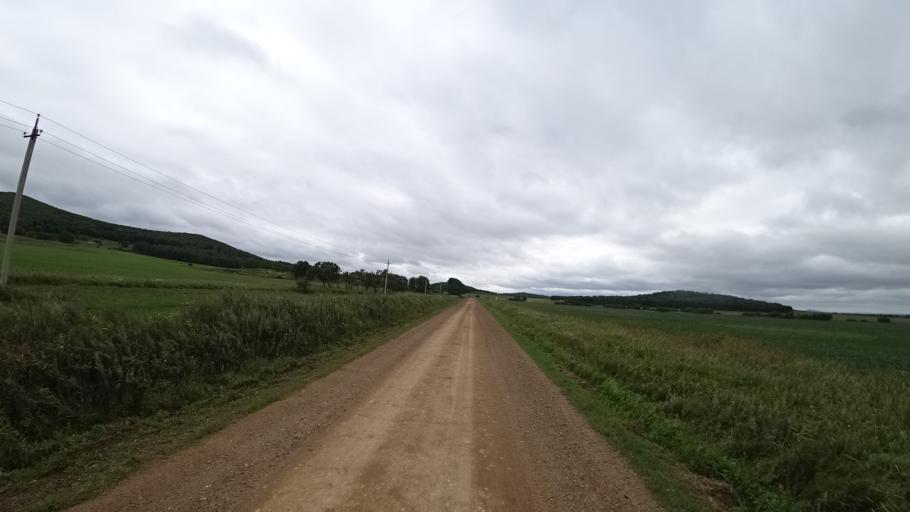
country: RU
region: Primorskiy
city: Chernigovka
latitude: 44.4741
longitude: 132.5804
